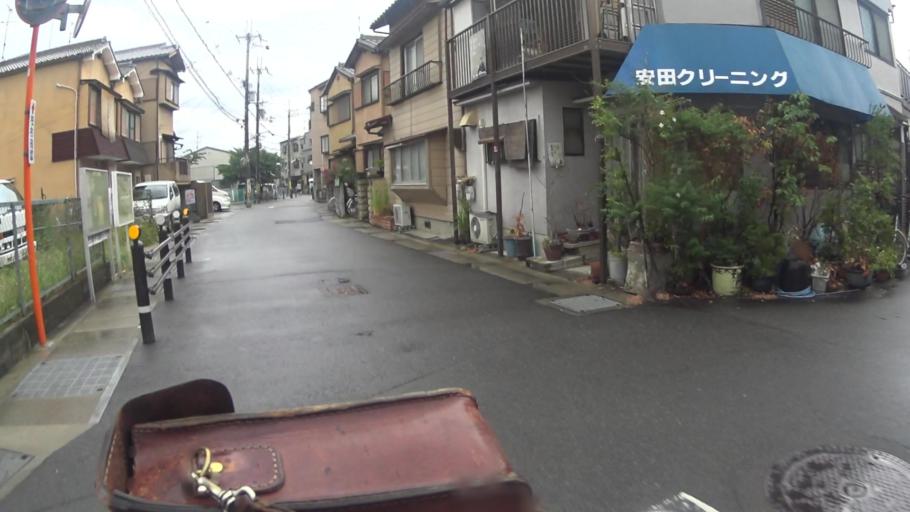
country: JP
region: Kyoto
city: Muko
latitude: 34.9408
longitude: 135.7077
